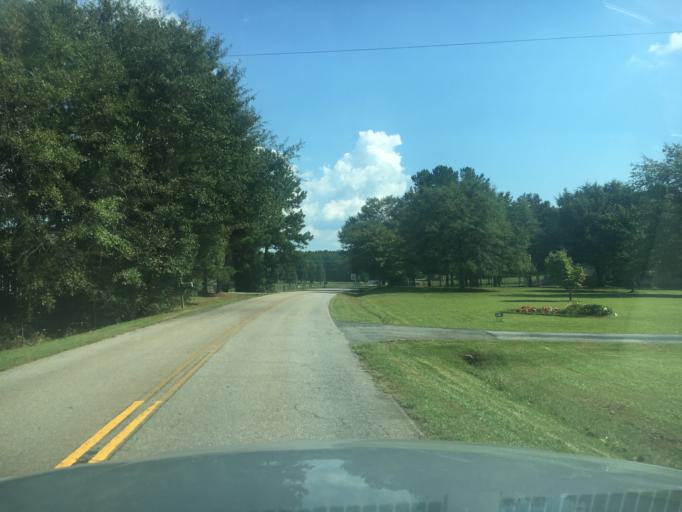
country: US
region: South Carolina
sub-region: Pickens County
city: Liberty
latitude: 34.7412
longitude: -82.6491
